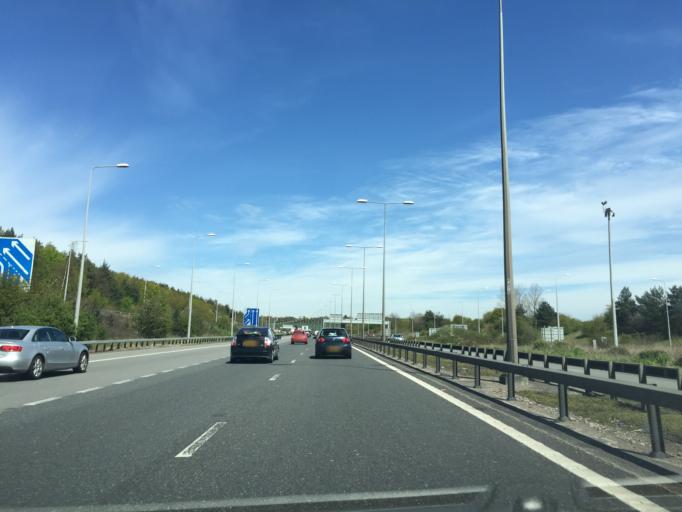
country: GB
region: England
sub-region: Essex
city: Epping
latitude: 51.6814
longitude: 0.1276
